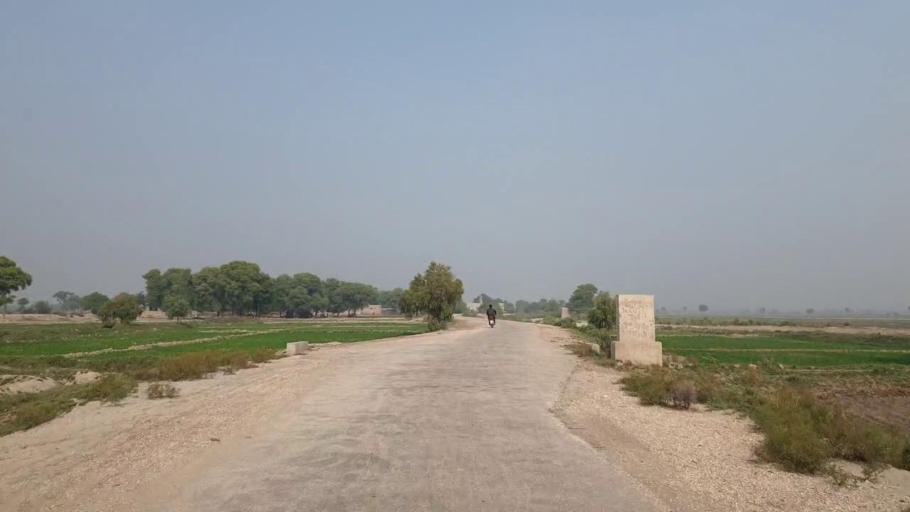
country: PK
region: Sindh
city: Bhan
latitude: 26.5217
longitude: 67.6905
